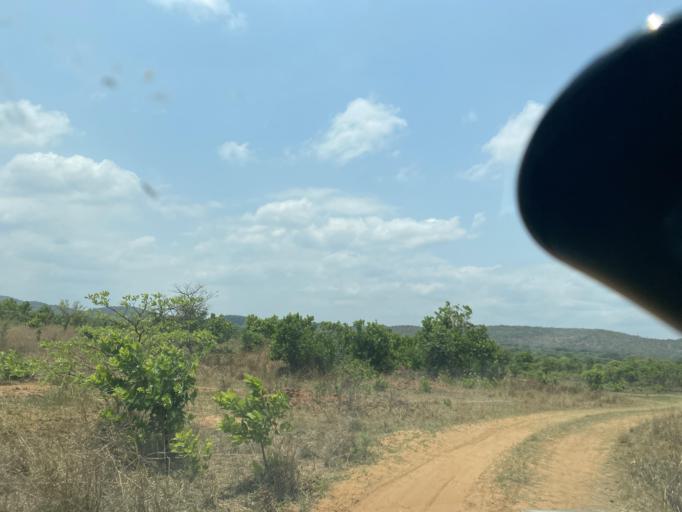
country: ZM
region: Lusaka
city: Chongwe
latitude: -15.5157
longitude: 28.8867
